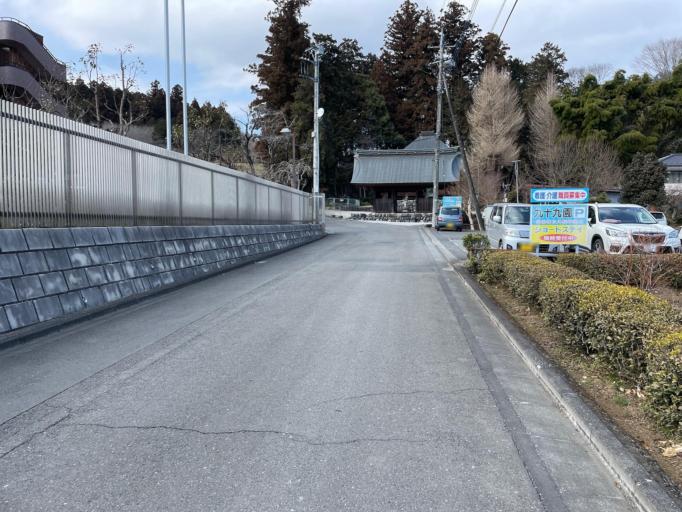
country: JP
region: Saitama
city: Hanno
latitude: 35.8384
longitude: 139.2779
